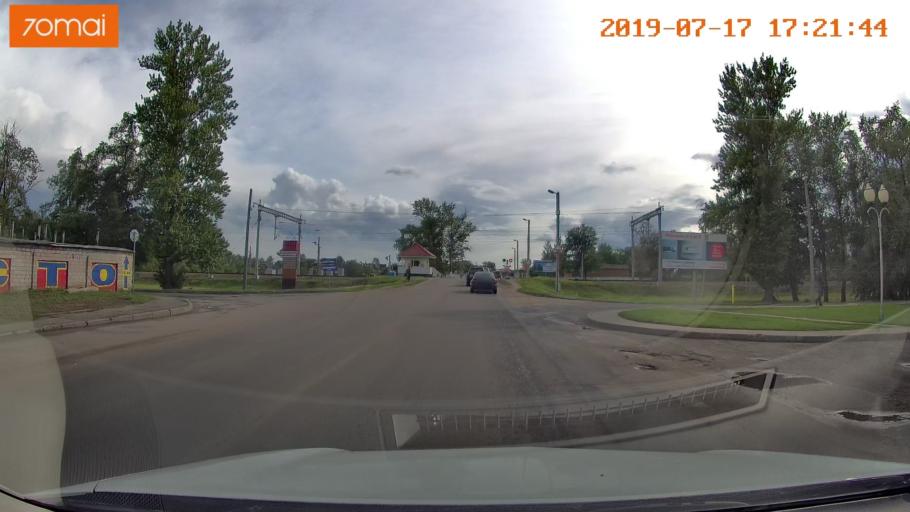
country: BY
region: Mogilev
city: Babruysk
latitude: 53.1468
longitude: 29.1775
